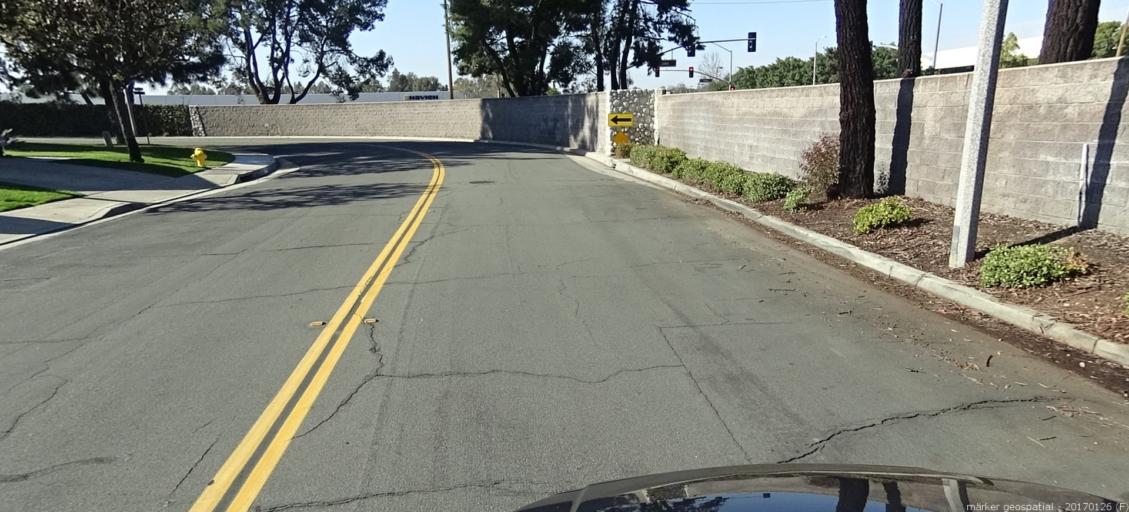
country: US
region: California
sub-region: Orange County
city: Lake Forest
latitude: 33.6494
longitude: -117.7066
